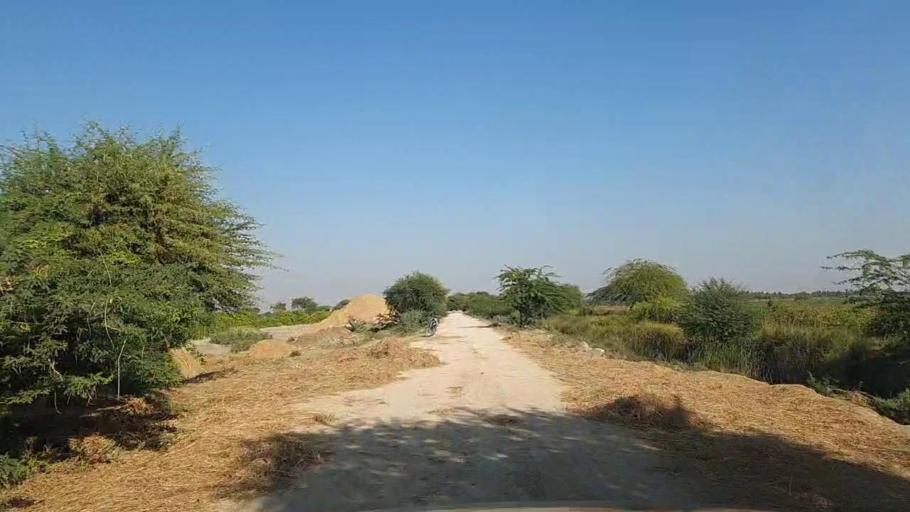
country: PK
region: Sindh
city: Mirpur Batoro
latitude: 24.7255
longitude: 68.3349
